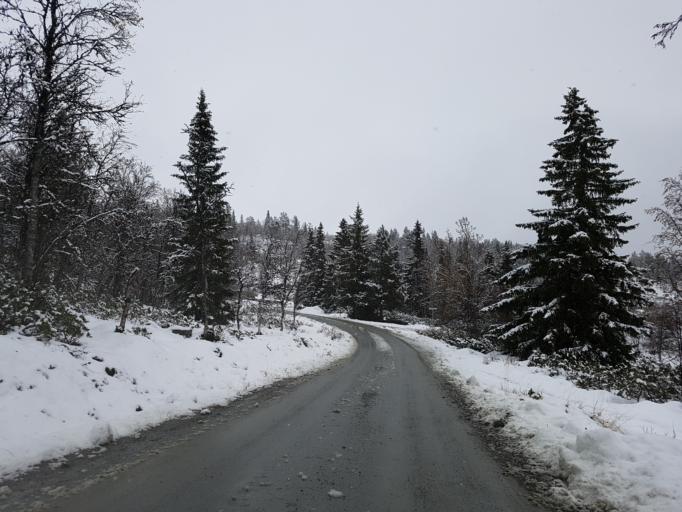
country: NO
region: Oppland
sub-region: Sel
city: Otta
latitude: 61.8019
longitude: 9.7057
